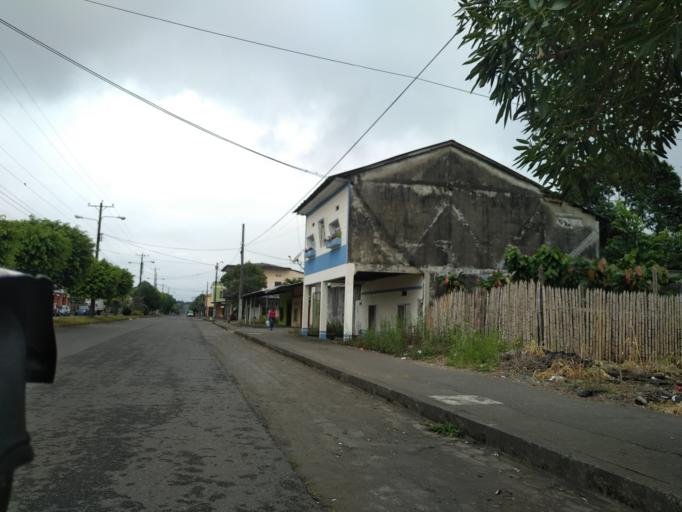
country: EC
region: Cotopaxi
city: La Mana
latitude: -0.9545
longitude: -79.3508
